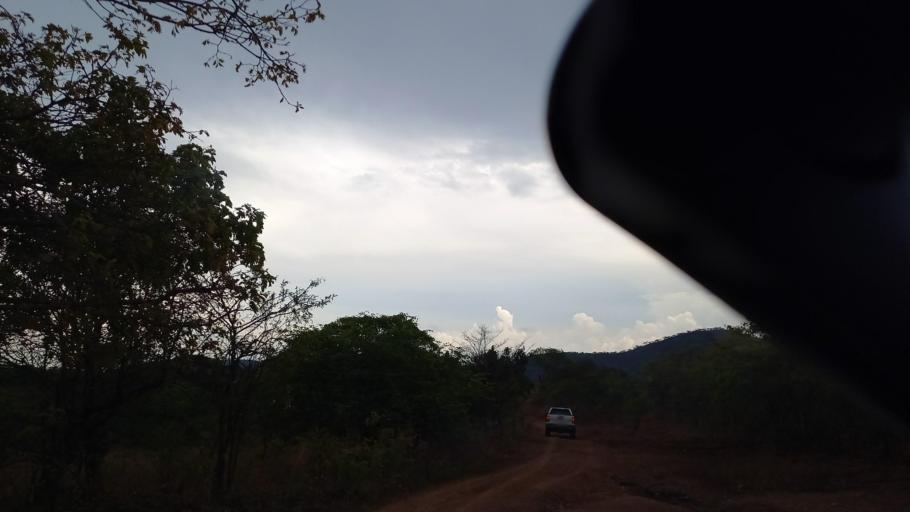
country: ZM
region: Lusaka
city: Kafue
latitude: -16.0278
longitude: 28.2988
